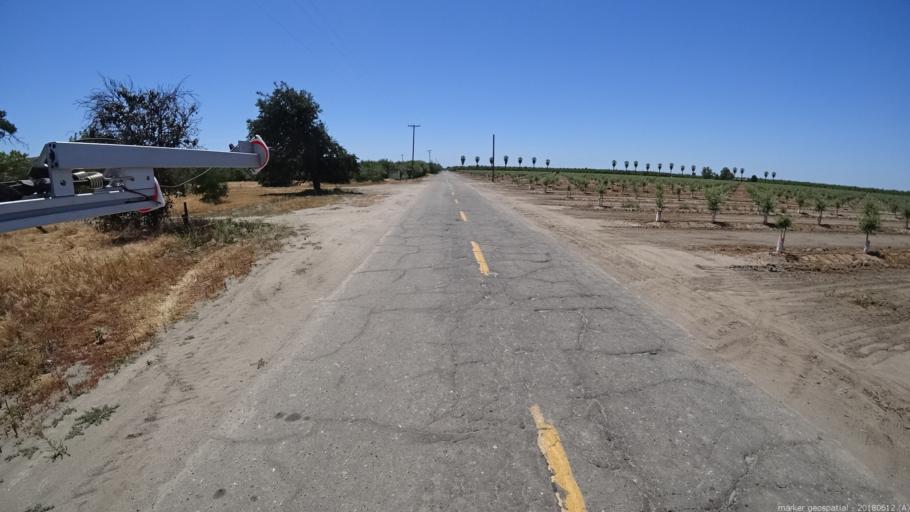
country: US
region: California
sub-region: Madera County
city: Chowchilla
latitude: 37.0617
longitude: -120.2885
